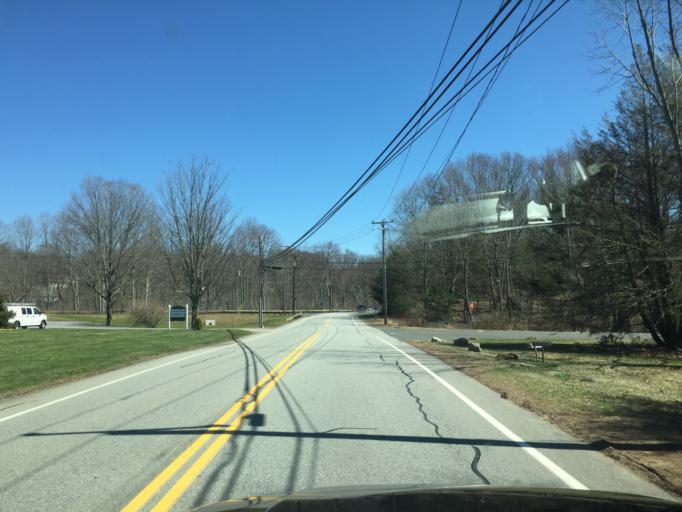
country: US
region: Connecticut
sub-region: Hartford County
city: Terramuggus
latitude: 41.6465
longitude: -72.4804
